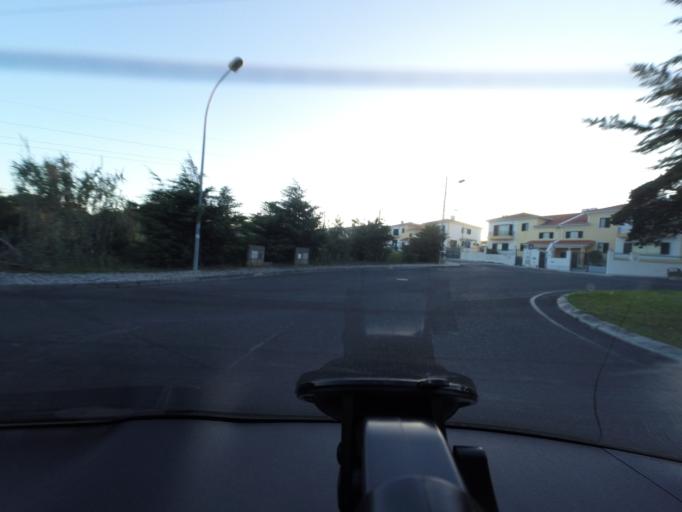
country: PT
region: Lisbon
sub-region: Sintra
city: Rio de Mouro
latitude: 38.7570
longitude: -9.3586
